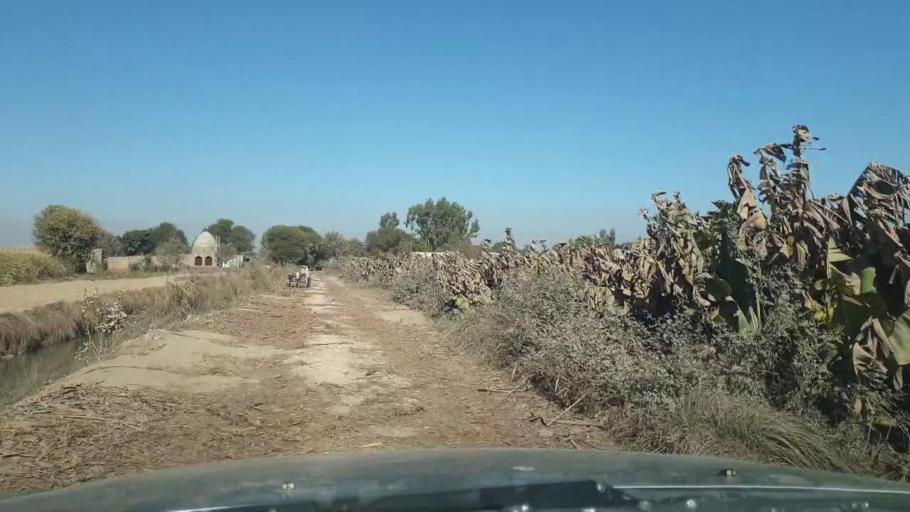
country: PK
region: Sindh
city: Ghotki
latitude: 28.0417
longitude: 69.2468
